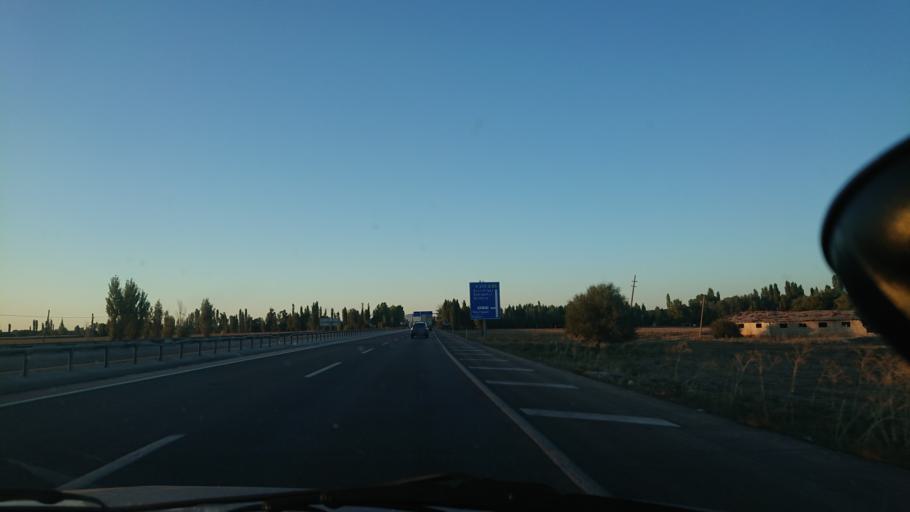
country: TR
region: Eskisehir
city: Mahmudiye
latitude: 39.5654
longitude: 30.9146
